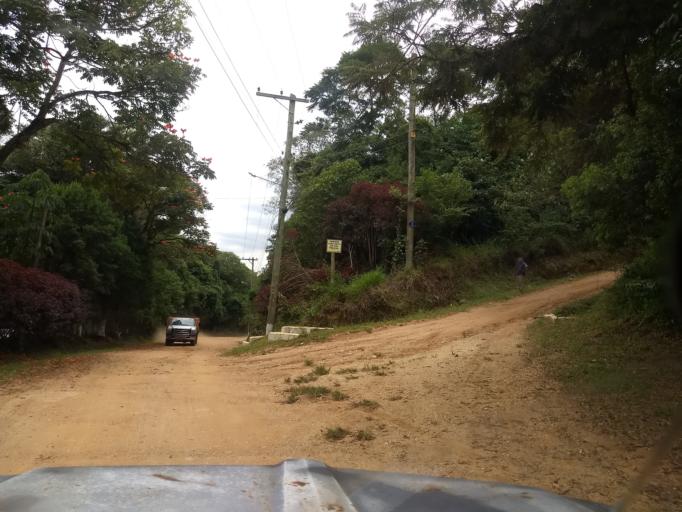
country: BR
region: Sao Paulo
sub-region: Cabreuva
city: Cabreuva
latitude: -23.3849
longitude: -47.1738
